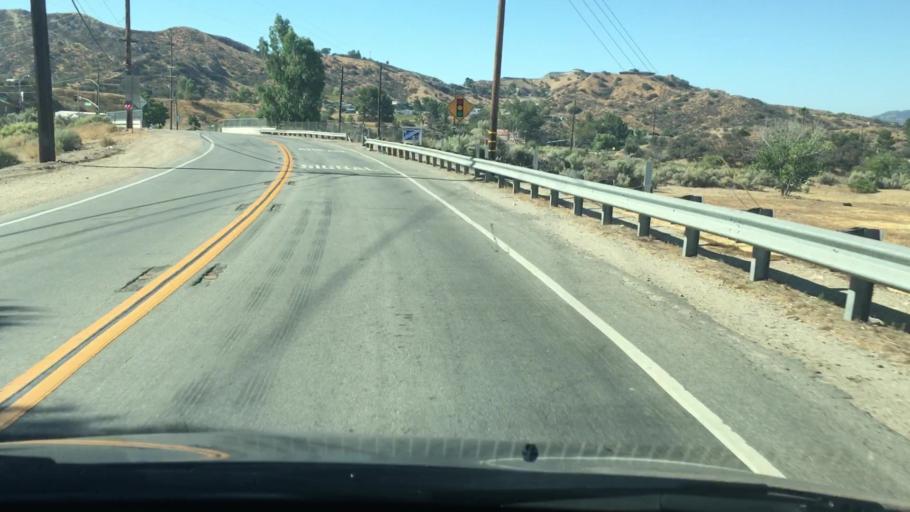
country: US
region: California
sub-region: Los Angeles County
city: Agua Dulce
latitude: 34.4557
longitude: -118.4215
